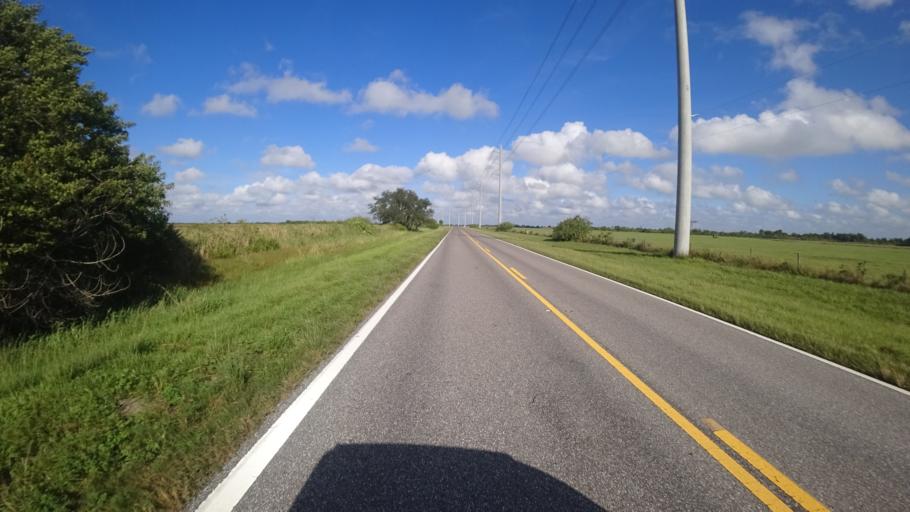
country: US
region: Florida
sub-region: Hillsborough County
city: Wimauma
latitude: 27.5165
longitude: -82.3255
